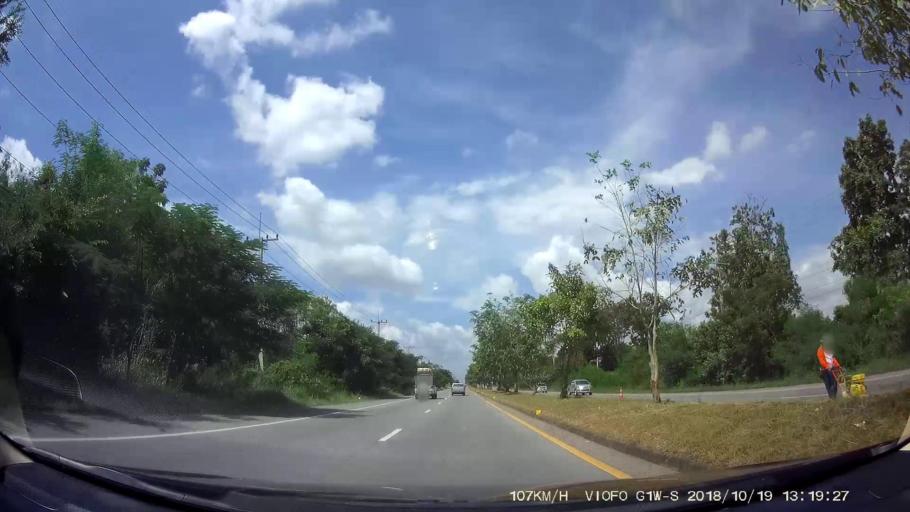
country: TH
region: Chaiyaphum
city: Chatturat
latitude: 15.4300
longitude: 101.8310
